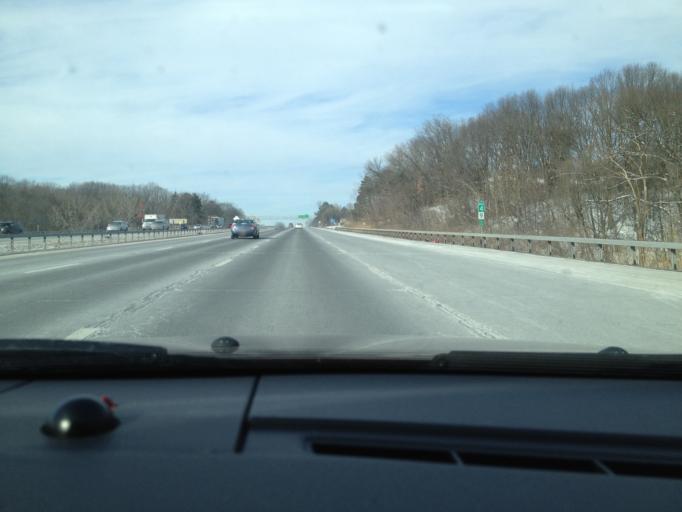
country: US
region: New York
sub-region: Albany County
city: Albany
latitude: 42.6720
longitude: -73.7557
